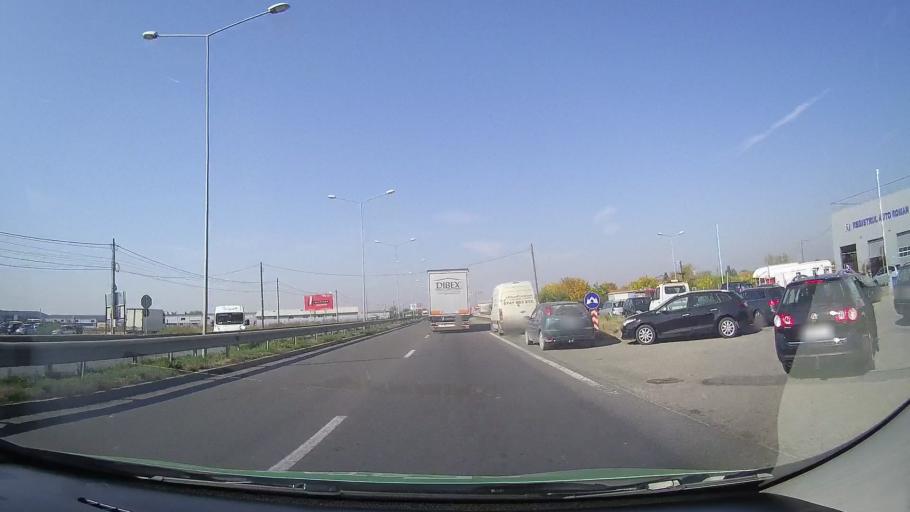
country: RO
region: Bihor
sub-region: Comuna Santandrei
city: Santandrei
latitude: 47.0483
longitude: 21.8923
